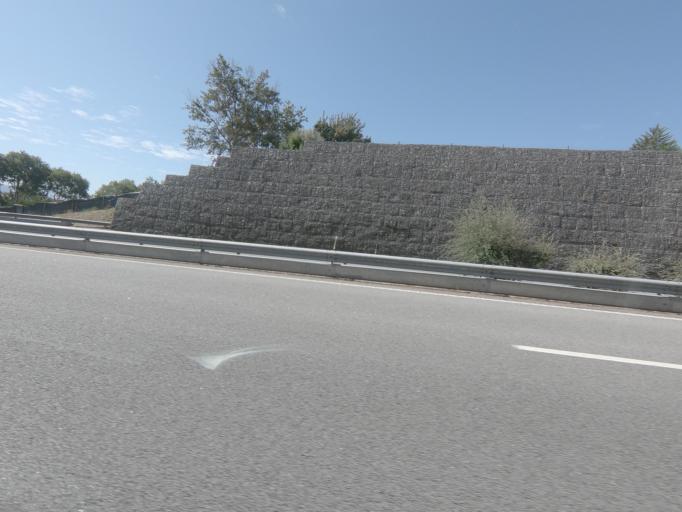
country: PT
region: Porto
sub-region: Marco de Canaveses
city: Marco de Canavezes
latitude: 41.2362
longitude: -8.1871
